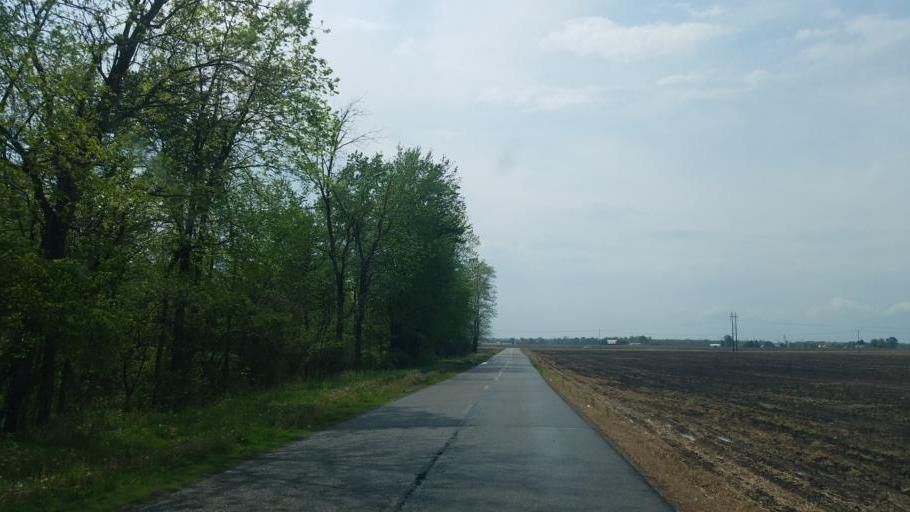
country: US
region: Ohio
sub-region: Fairfield County
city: Millersport
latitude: 39.9204
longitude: -82.5285
